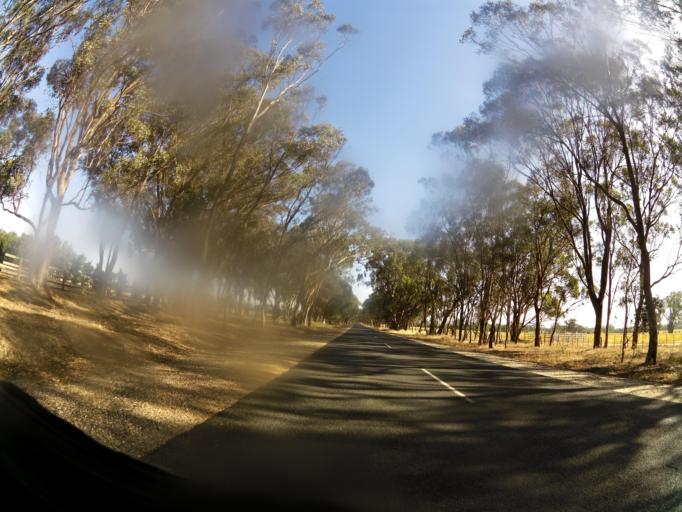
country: AU
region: Victoria
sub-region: Murrindindi
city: Kinglake West
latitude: -36.9669
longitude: 145.1087
